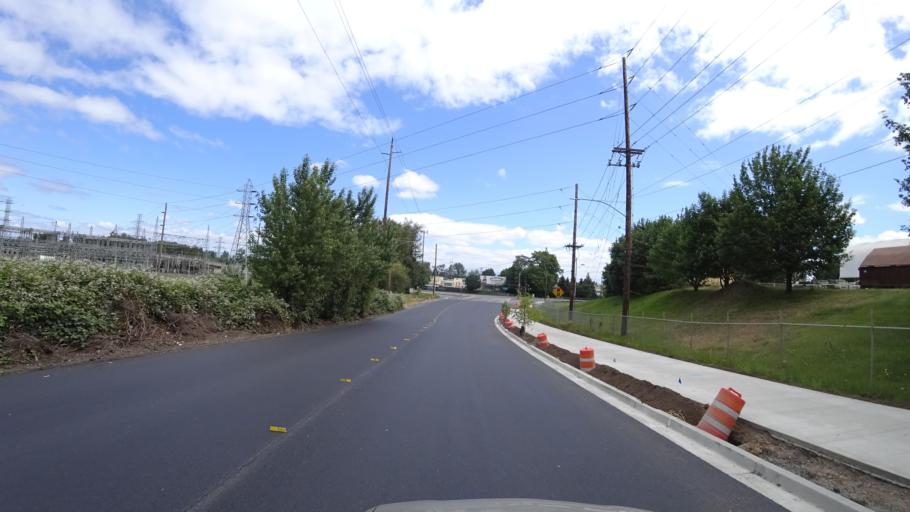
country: US
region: Oregon
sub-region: Washington County
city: West Haven
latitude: 45.6121
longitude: -122.7649
